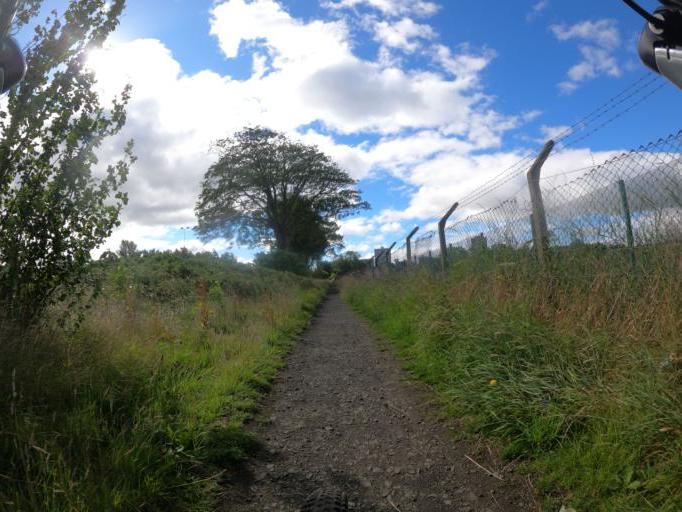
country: GB
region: Scotland
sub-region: Edinburgh
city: Edinburgh
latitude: 55.9770
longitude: -3.2611
